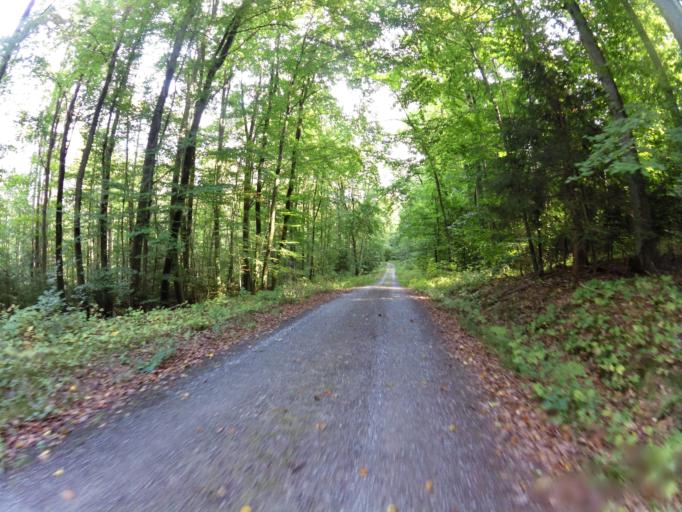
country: DE
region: Bavaria
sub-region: Regierungsbezirk Unterfranken
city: Waldbrunn
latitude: 49.7455
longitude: 9.8065
